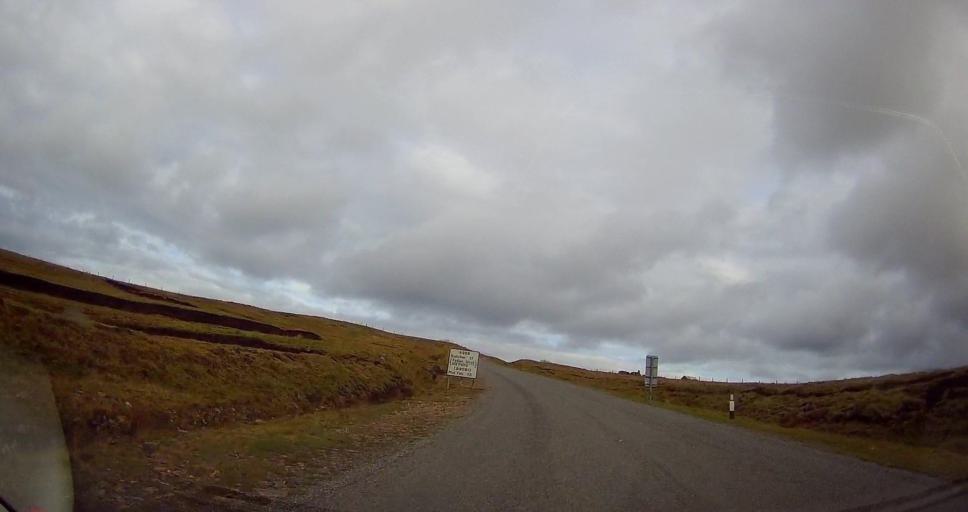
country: GB
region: Scotland
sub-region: Shetland Islands
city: Shetland
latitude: 60.5002
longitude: -1.1581
